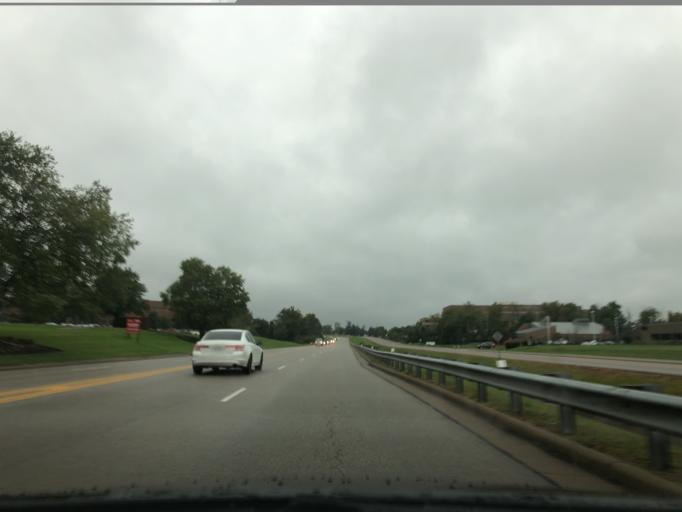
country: US
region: Ohio
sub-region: Hamilton County
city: Blue Ash
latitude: 39.2448
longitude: -84.3833
